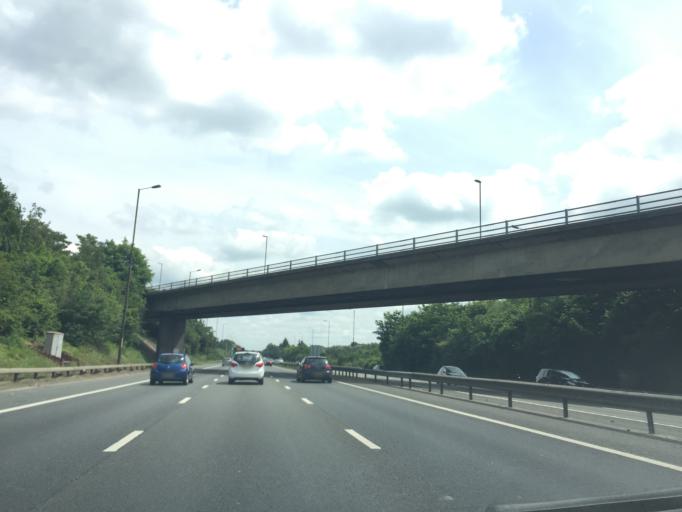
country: GB
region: England
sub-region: Kent
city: Dartford
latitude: 51.4315
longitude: 0.1999
